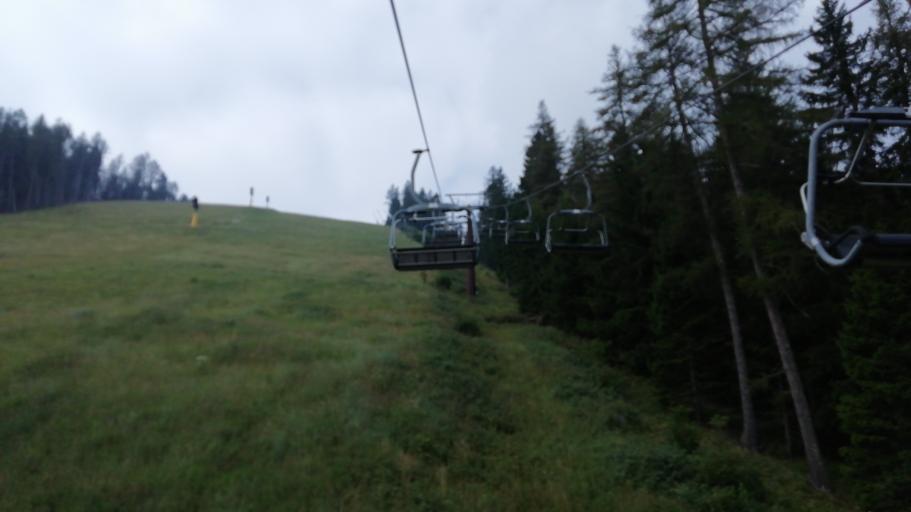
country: IT
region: Trentino-Alto Adige
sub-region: Provincia di Trento
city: Piazza
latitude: 45.8905
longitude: 11.1839
